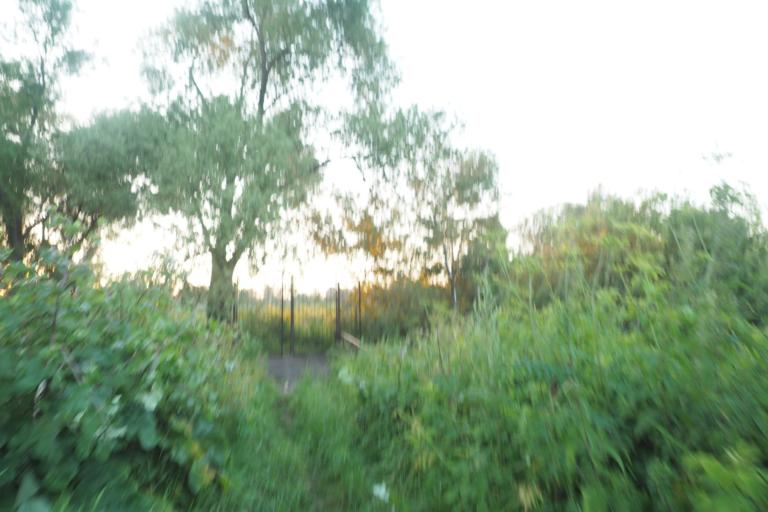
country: RU
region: Moskovskaya
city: Malyshevo
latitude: 55.5528
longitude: 38.3188
